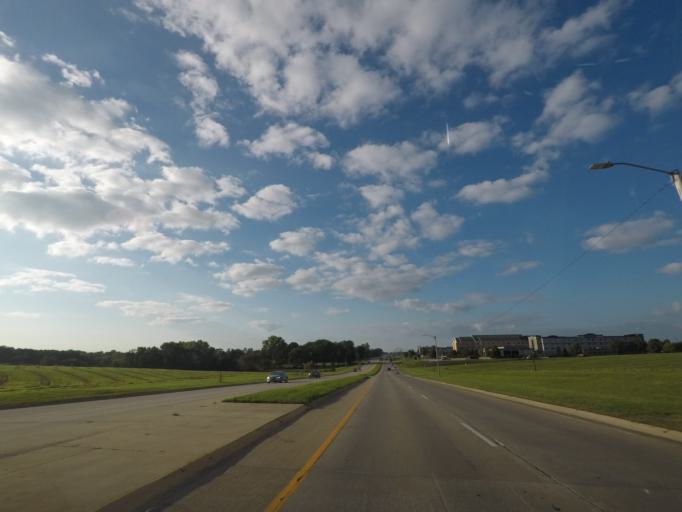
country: US
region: Iowa
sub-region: Warren County
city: Norwalk
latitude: 41.5249
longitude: -93.6449
